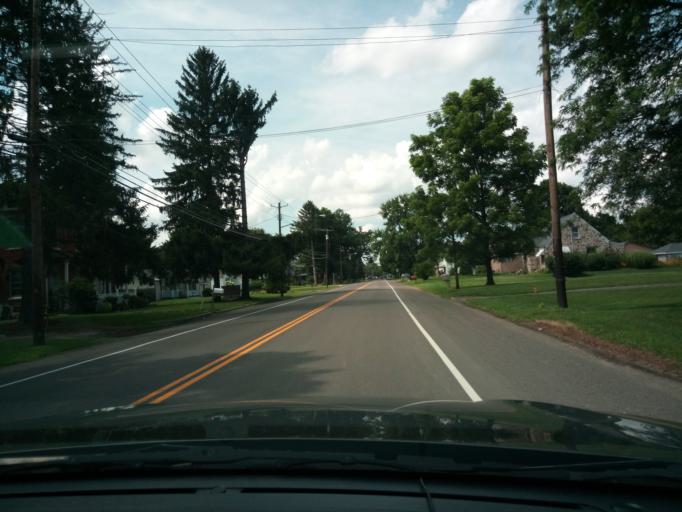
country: US
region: New York
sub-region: Chemung County
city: Southport
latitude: 42.0573
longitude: -76.7823
